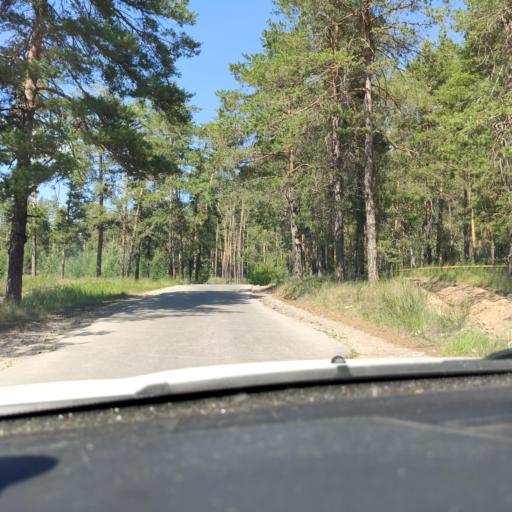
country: RU
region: Samara
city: Pribrezhnyy
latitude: 53.4797
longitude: 49.8251
